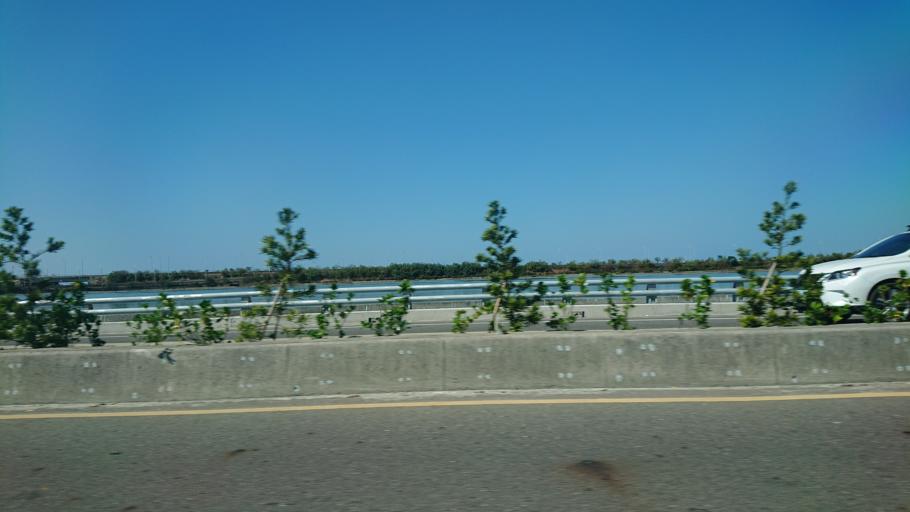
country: TW
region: Taiwan
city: Xinying
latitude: 23.2802
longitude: 120.1315
